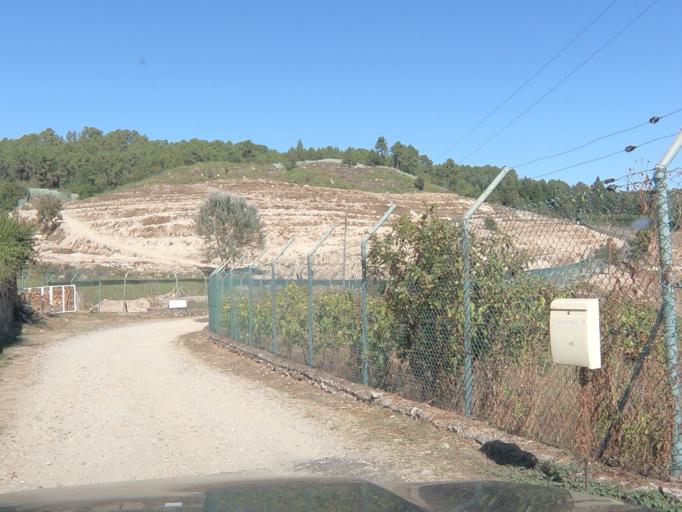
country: PT
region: Vila Real
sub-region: Vila Real
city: Vila Real
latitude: 41.3216
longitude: -7.7241
